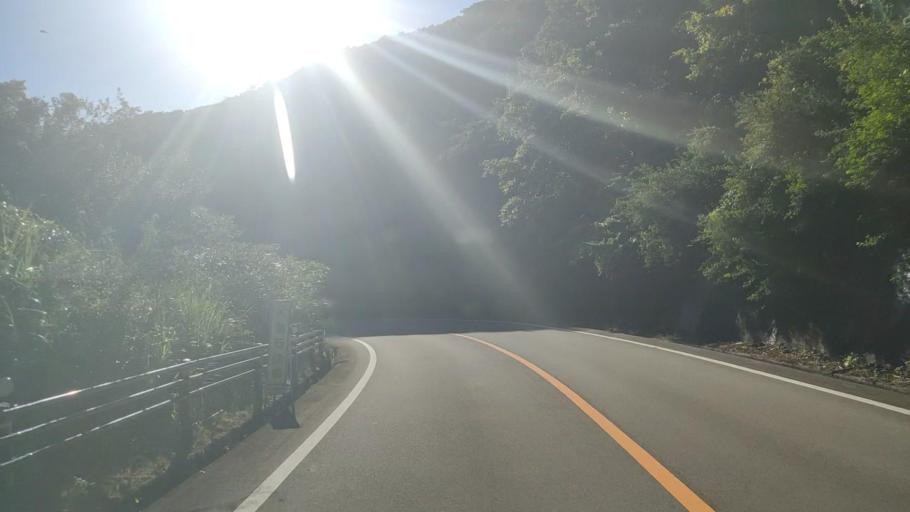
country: JP
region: Mie
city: Toba
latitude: 34.3995
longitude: 136.8671
